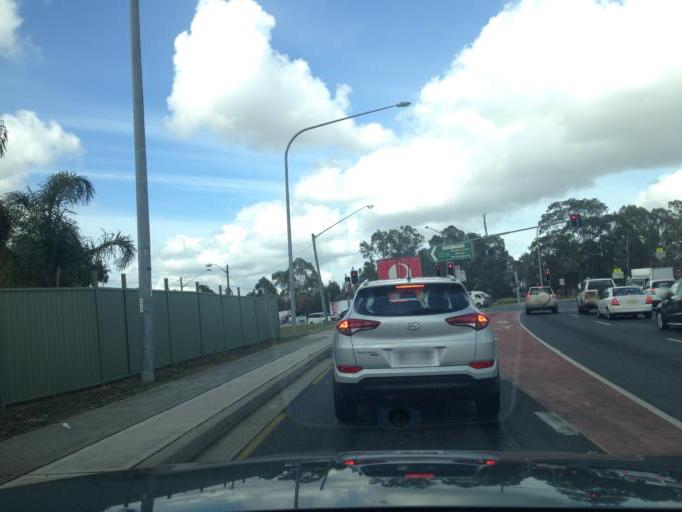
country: AU
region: New South Wales
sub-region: Bankstown
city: Bankstown
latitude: -33.9058
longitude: 151.0408
